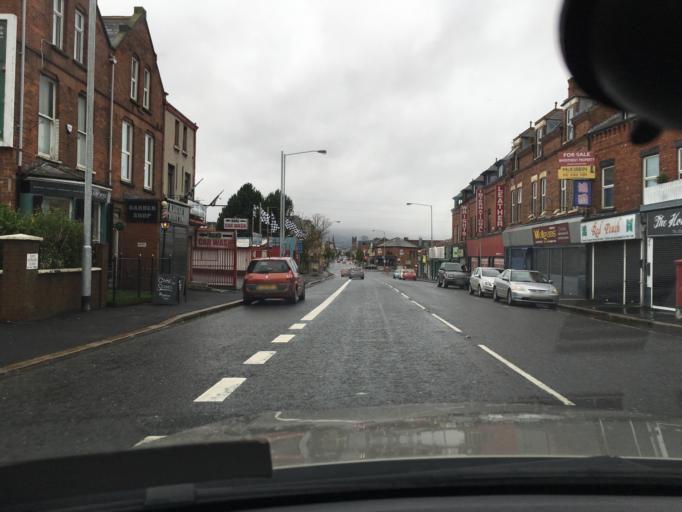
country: GB
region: Northern Ireland
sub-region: Castlereagh District
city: Castlereagh
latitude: 54.5973
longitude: -5.8859
